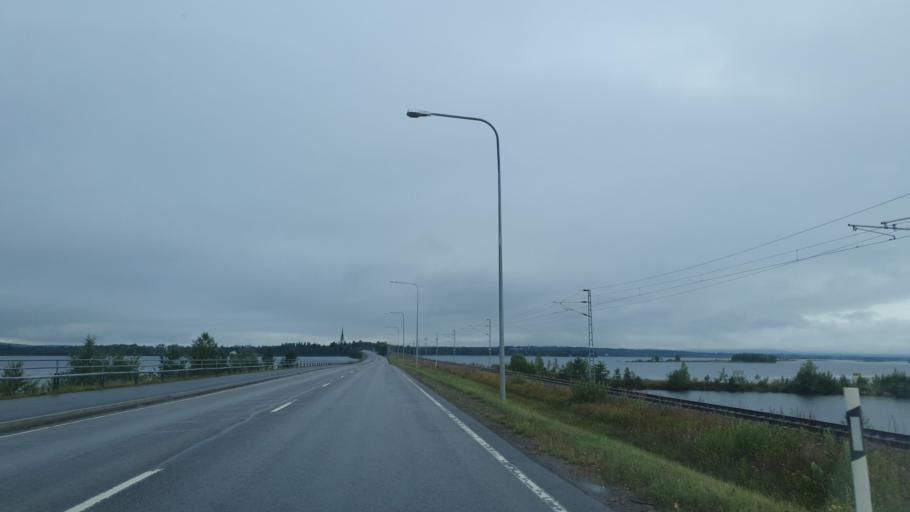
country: FI
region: Lapland
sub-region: Itae-Lappi
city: Kemijaervi
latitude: 66.7158
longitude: 27.4714
